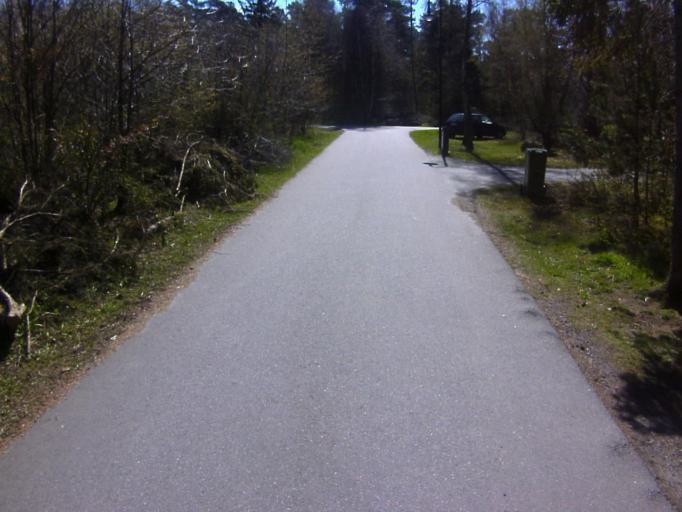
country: SE
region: Skane
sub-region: Kavlinge Kommun
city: Hofterup
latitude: 55.8097
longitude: 12.9828
